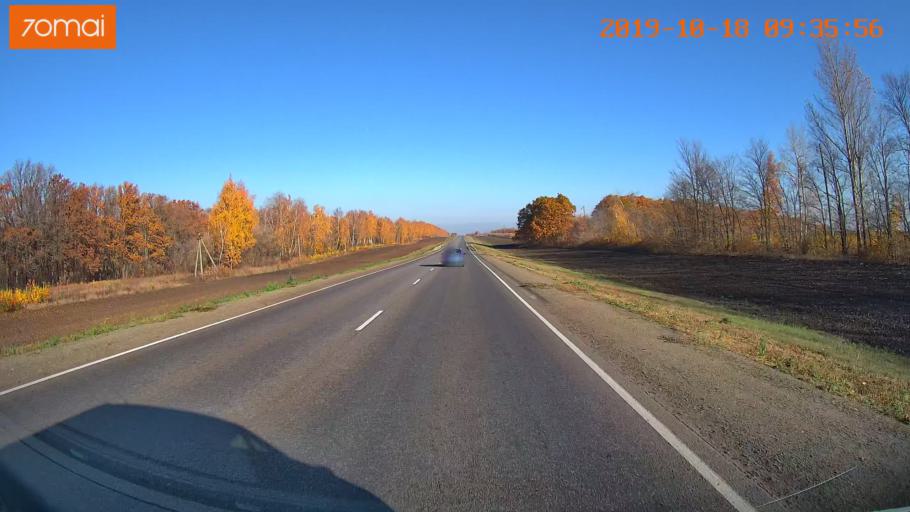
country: RU
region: Tula
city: Yefremov
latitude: 53.1989
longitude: 38.1469
